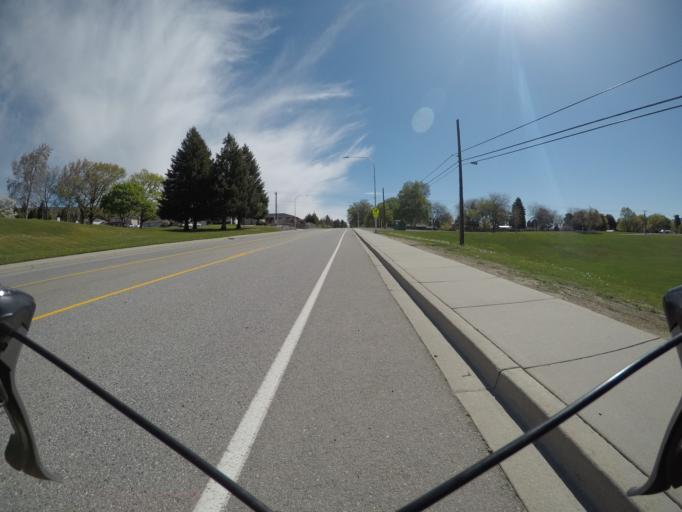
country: US
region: Washington
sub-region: Douglas County
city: East Wenatchee Bench
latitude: 47.4166
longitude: -120.2705
